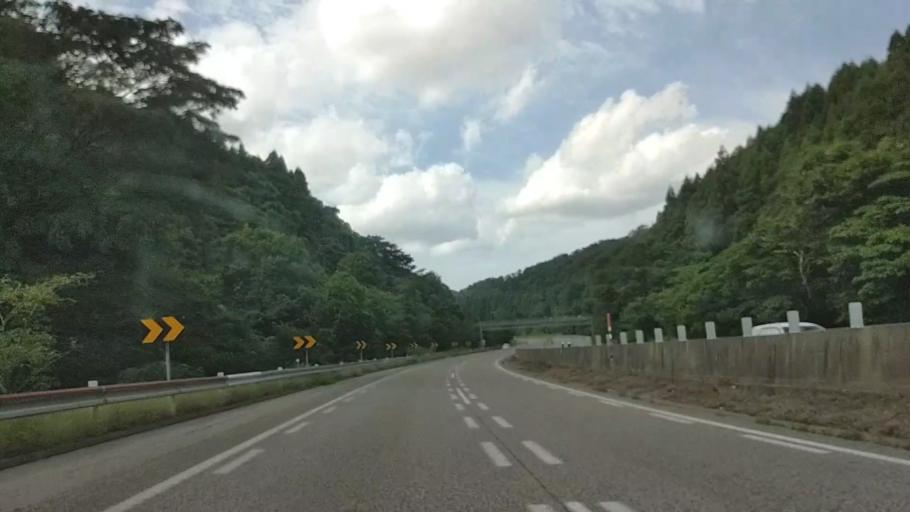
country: JP
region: Ishikawa
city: Tsubata
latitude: 36.5969
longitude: 136.7495
